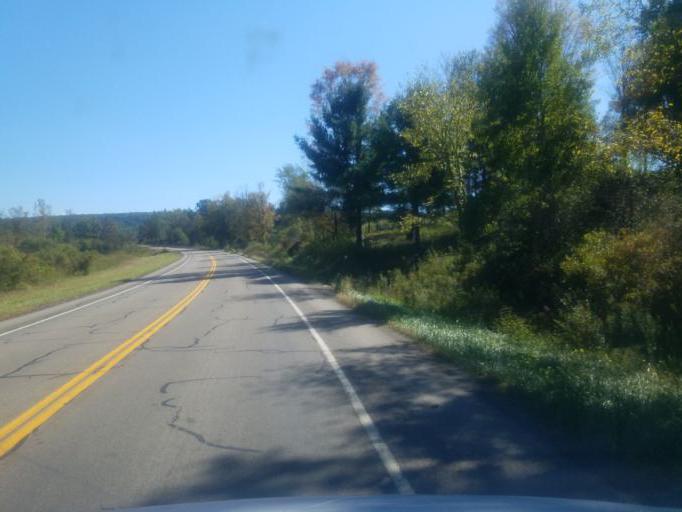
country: US
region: New York
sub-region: Allegany County
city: Friendship
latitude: 42.3019
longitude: -78.1622
